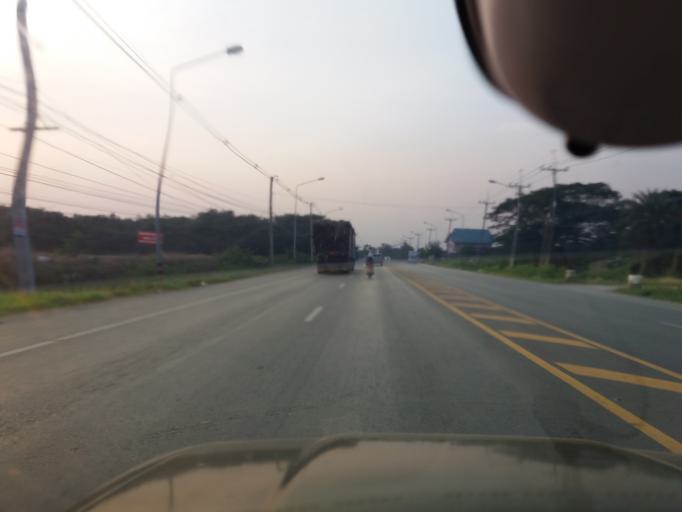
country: TH
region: Sing Buri
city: Sing Buri
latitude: 14.8851
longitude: 100.3764
